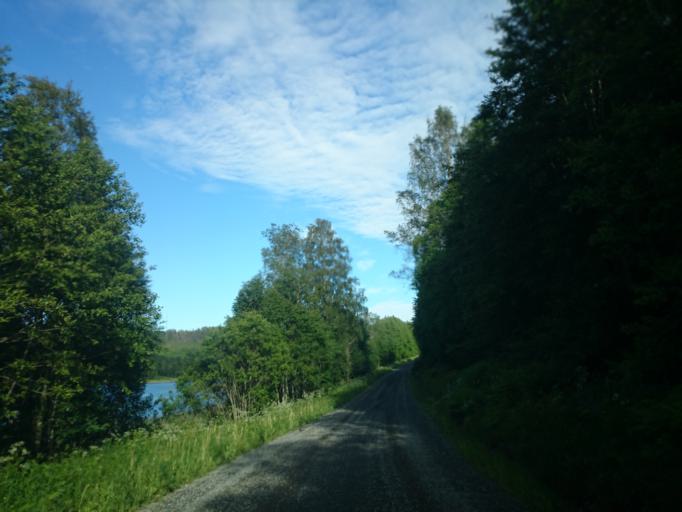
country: SE
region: Vaesternorrland
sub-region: Haernoesands Kommun
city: Haernoesand
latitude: 62.6242
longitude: 17.8605
